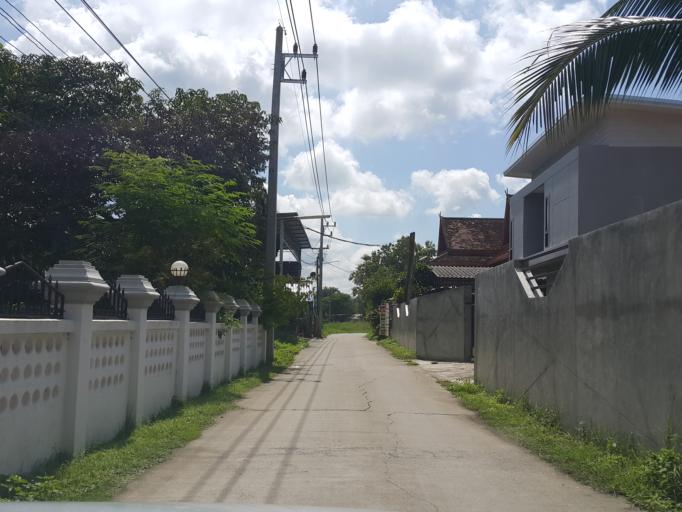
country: TH
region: Chiang Mai
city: San Kamphaeng
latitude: 18.7462
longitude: 99.1124
